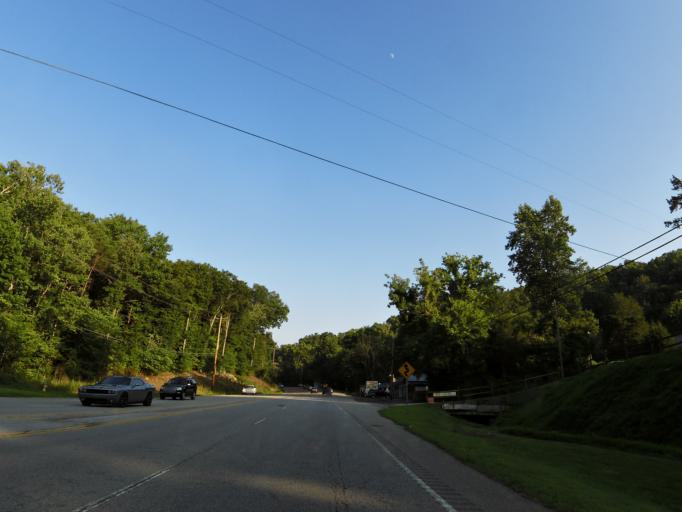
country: US
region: Tennessee
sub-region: Anderson County
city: Clinton
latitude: 36.0298
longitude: -84.0924
